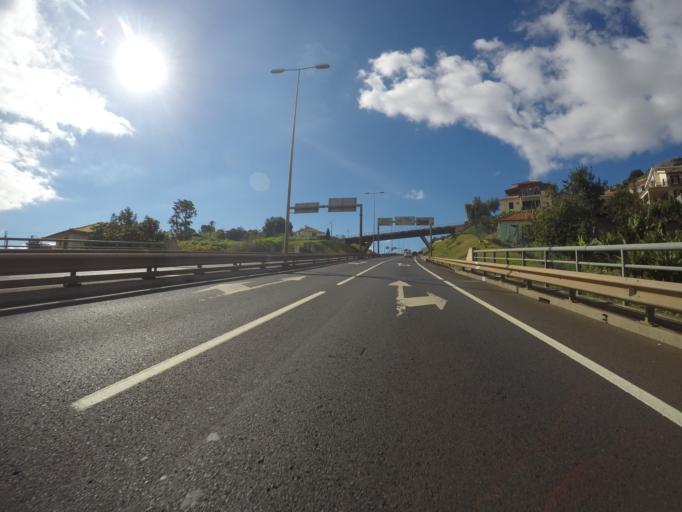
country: PT
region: Madeira
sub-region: Funchal
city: Nossa Senhora do Monte
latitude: 32.6584
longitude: -16.9344
